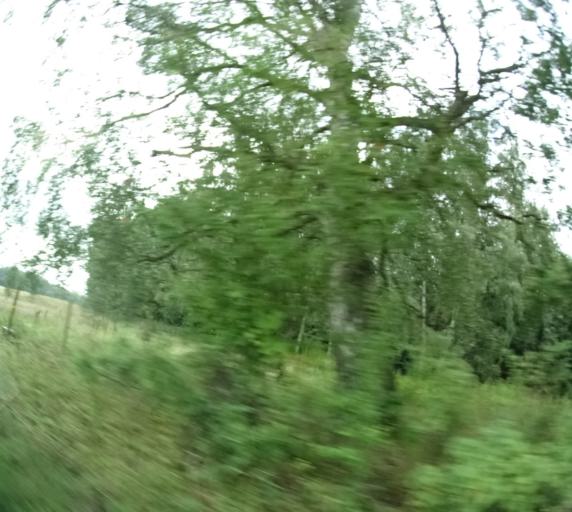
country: DK
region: Central Jutland
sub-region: Syddjurs Kommune
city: Ryomgard
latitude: 56.4030
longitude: 10.5169
